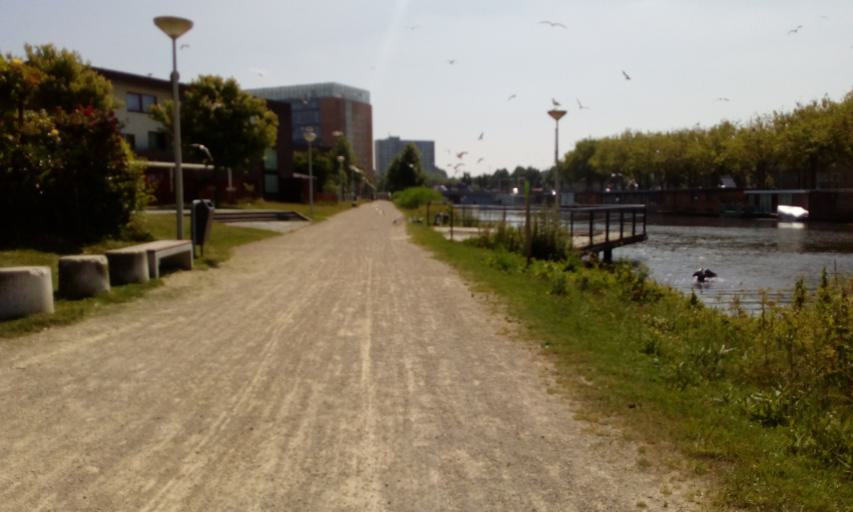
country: NL
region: South Holland
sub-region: Gemeente Den Haag
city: The Hague
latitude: 52.0580
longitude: 4.2991
